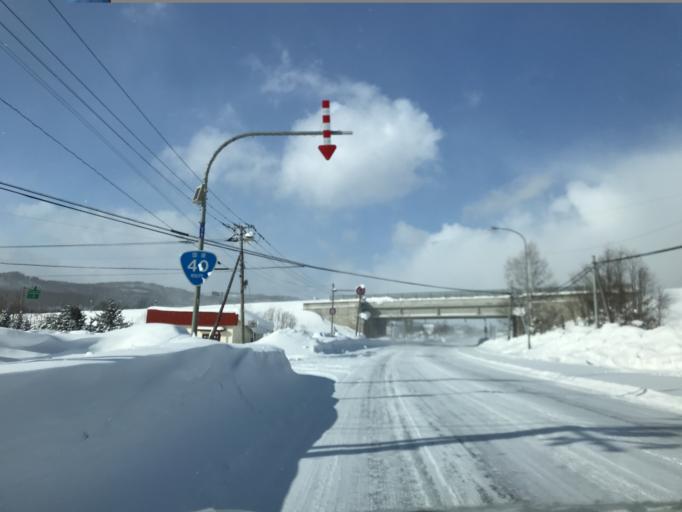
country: JP
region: Hokkaido
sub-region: Asahikawa-shi
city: Asahikawa
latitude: 43.9217
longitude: 142.4784
